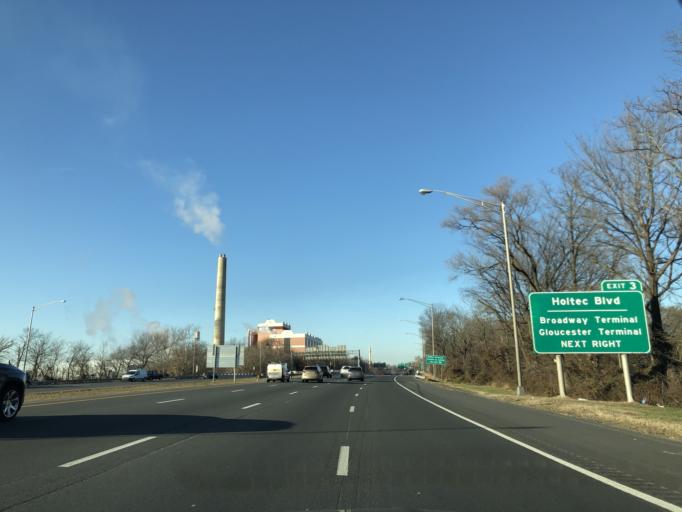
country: US
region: New Jersey
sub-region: Camden County
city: Gloucester City
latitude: 39.9054
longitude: -75.1131
